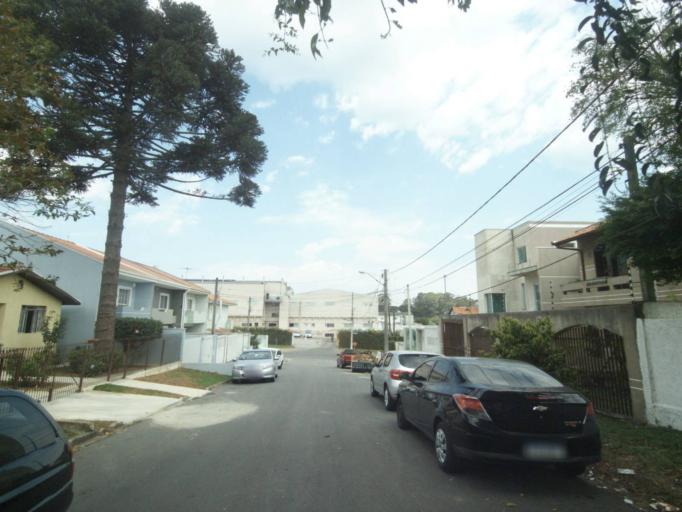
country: BR
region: Parana
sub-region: Sao Jose Dos Pinhais
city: Sao Jose dos Pinhais
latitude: -25.5176
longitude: -49.2568
